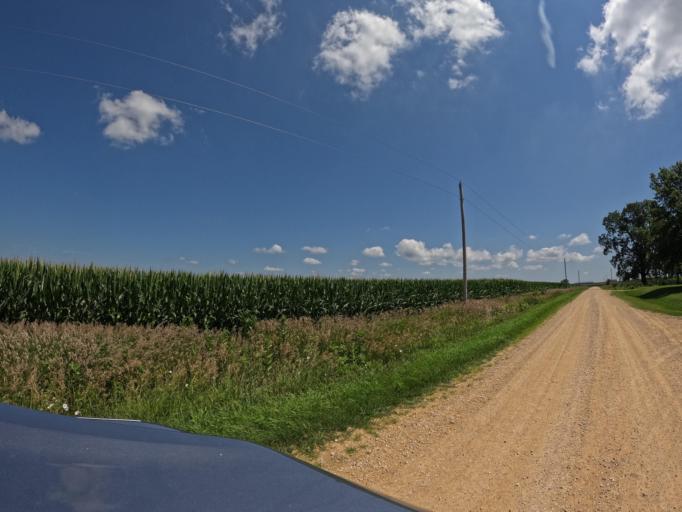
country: US
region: Iowa
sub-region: Clinton County
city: De Witt
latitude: 41.7783
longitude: -90.4178
